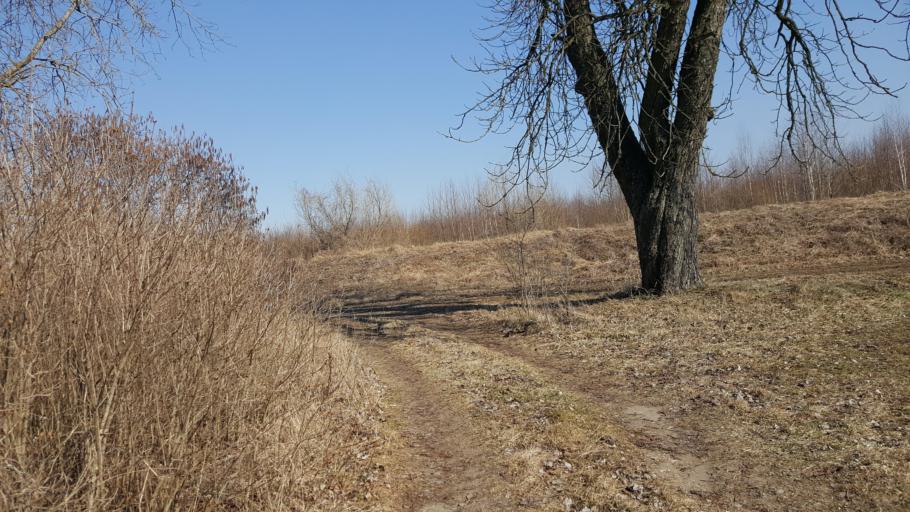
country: BY
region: Brest
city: Kamyanyets
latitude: 52.3629
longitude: 23.7445
